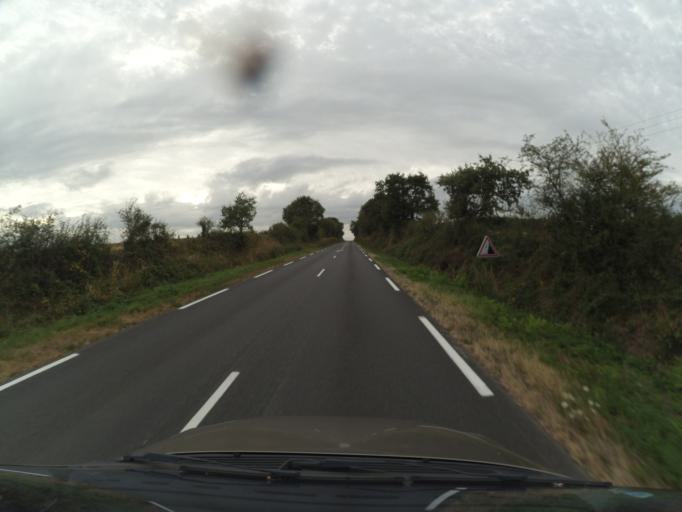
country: FR
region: Pays de la Loire
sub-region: Departement de Maine-et-Loire
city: Le Longeron
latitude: 47.0270
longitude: -1.0711
